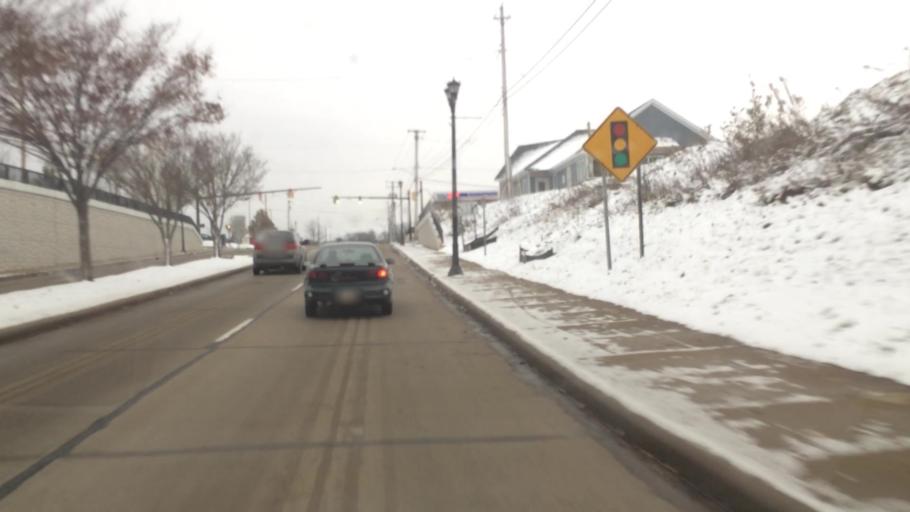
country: US
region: Ohio
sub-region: Cuyahoga County
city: Berea
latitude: 41.3722
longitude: -81.8714
